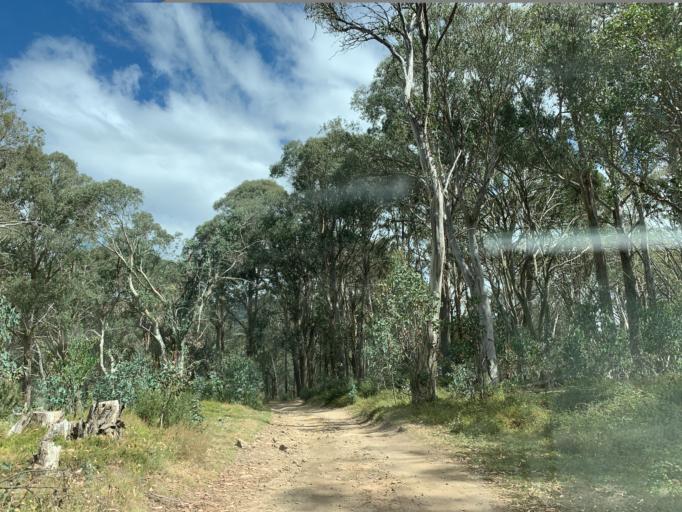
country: AU
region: Victoria
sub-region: Mansfield
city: Mansfield
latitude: -37.1038
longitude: 146.5382
